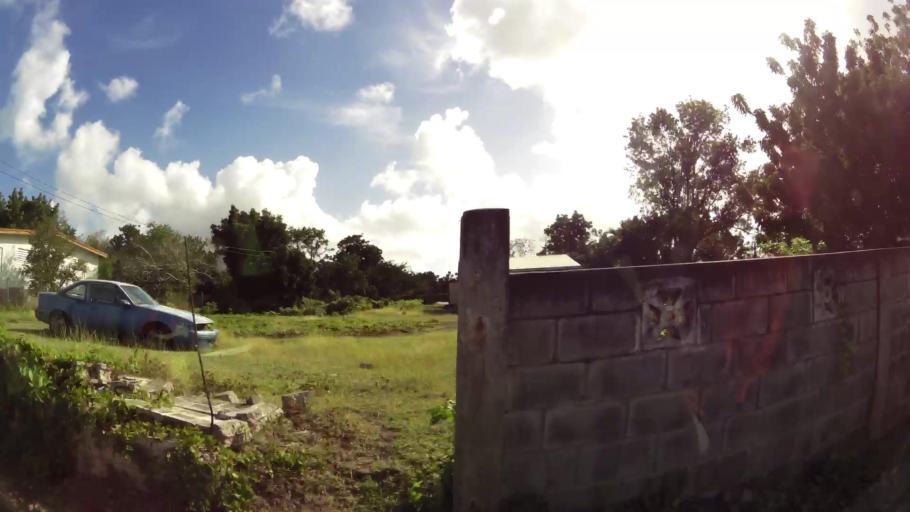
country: KN
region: Saint Paul Charlestown
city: Charlestown
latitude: 17.1299
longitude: -62.6296
